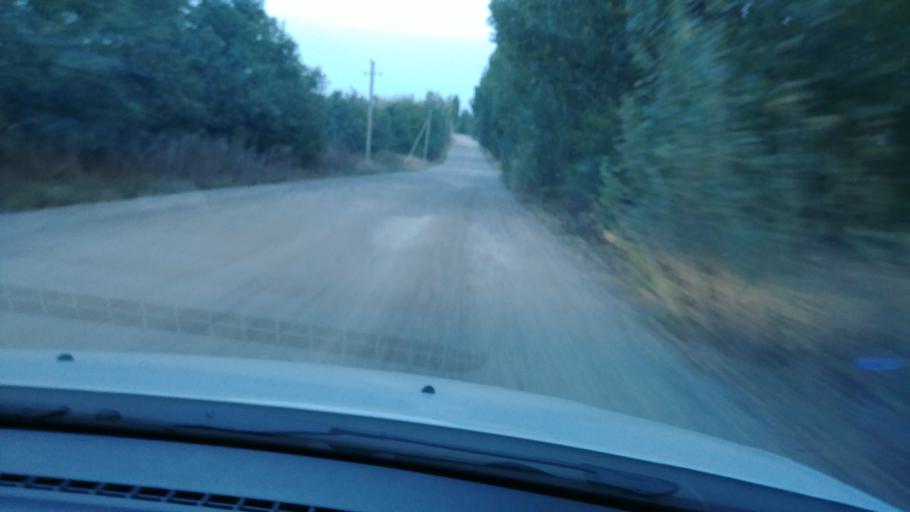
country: MD
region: Rezina
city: Saharna
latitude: 47.6781
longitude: 28.9230
